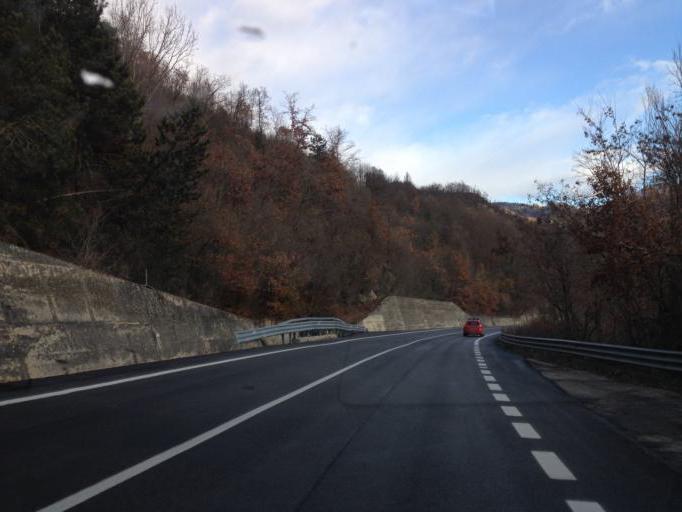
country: IT
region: The Marches
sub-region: Provincia di Ascoli Piceno
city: Arquata del Tronto
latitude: 42.7641
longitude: 13.2848
